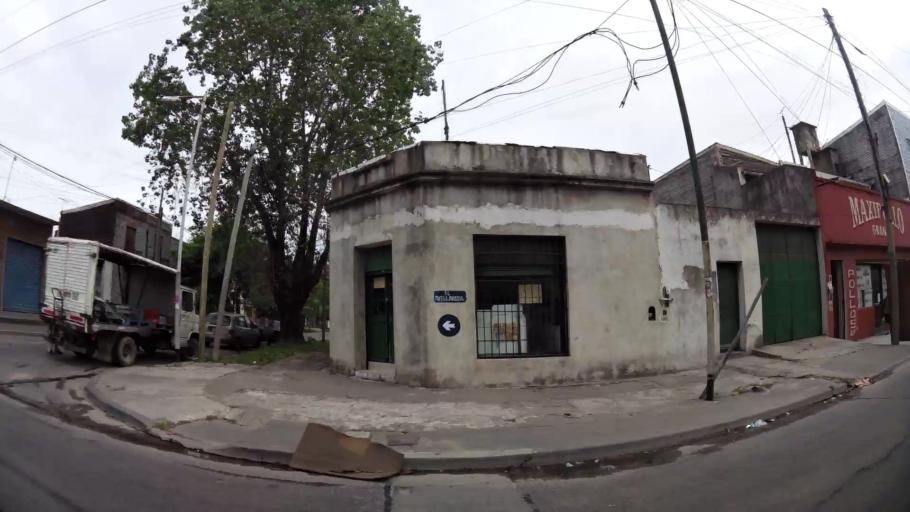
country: AR
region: Buenos Aires
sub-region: Partido de Avellaneda
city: Avellaneda
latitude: -34.6493
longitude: -58.3478
